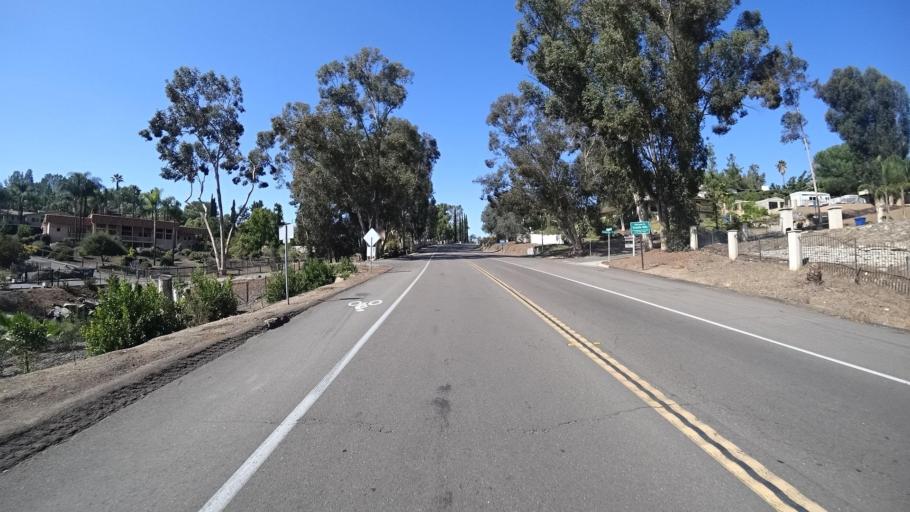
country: US
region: California
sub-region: San Diego County
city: Granite Hills
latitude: 32.7859
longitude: -116.8940
